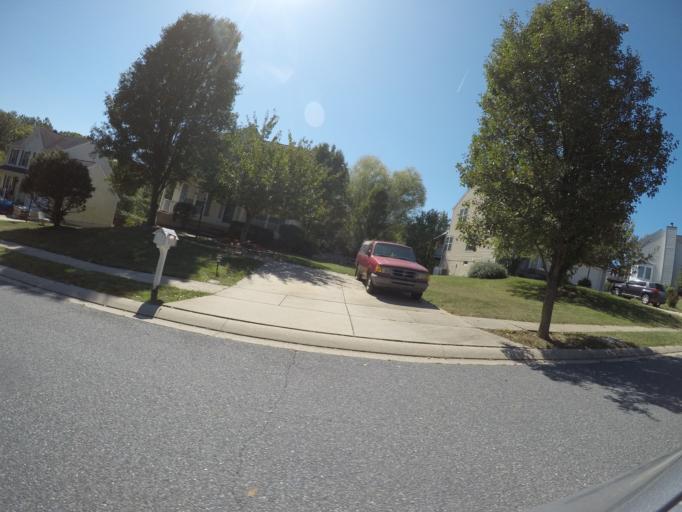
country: US
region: Maryland
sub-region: Harford County
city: Riverside
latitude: 39.4733
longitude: -76.2803
